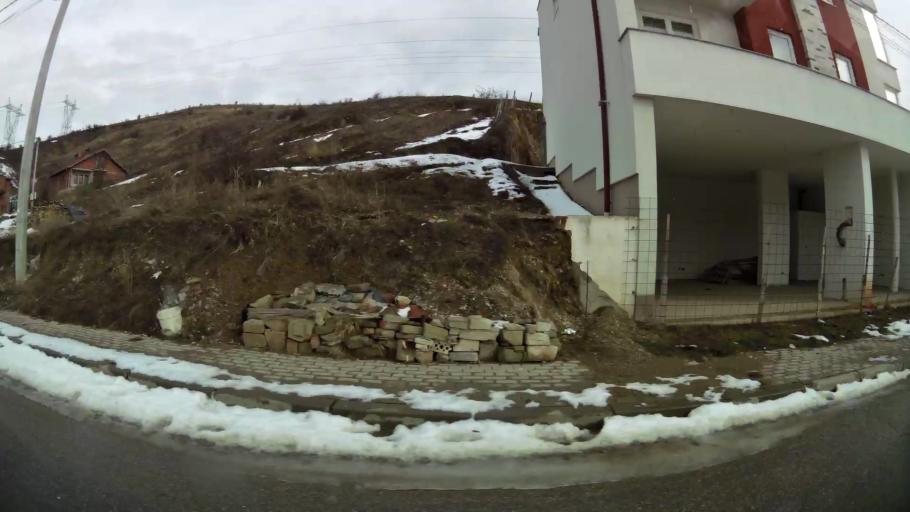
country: XK
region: Pristina
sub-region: Komuna e Prishtines
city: Pristina
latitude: 42.6915
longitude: 21.1761
